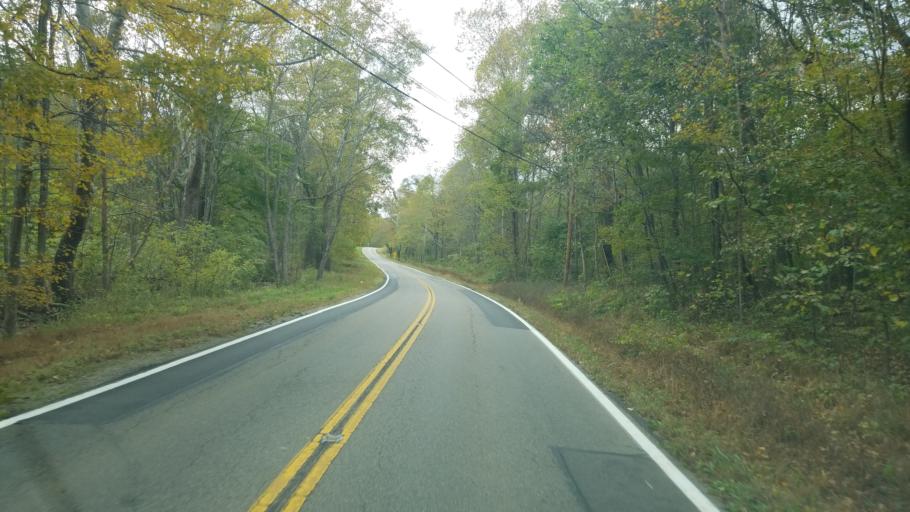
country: US
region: Ohio
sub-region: Jackson County
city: Jackson
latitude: 39.0725
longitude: -82.6037
